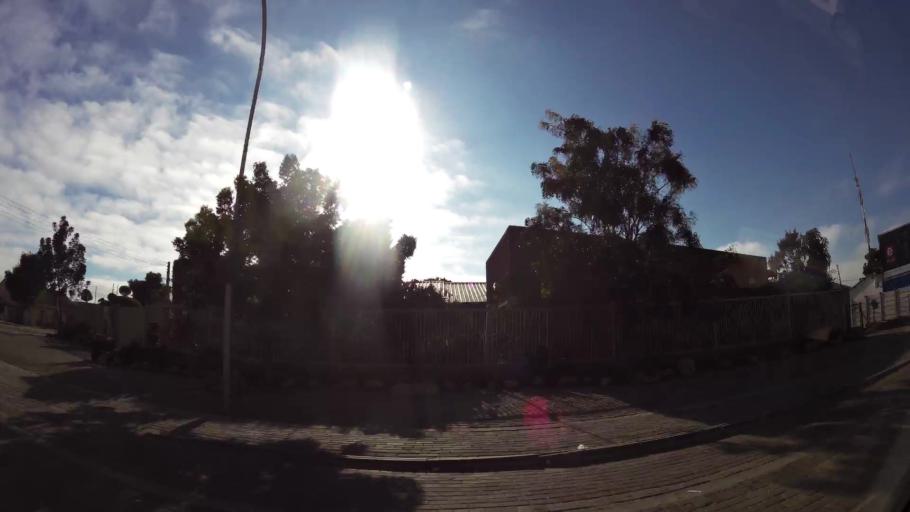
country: ZA
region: Limpopo
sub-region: Capricorn District Municipality
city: Polokwane
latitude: -23.8455
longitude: 29.3883
